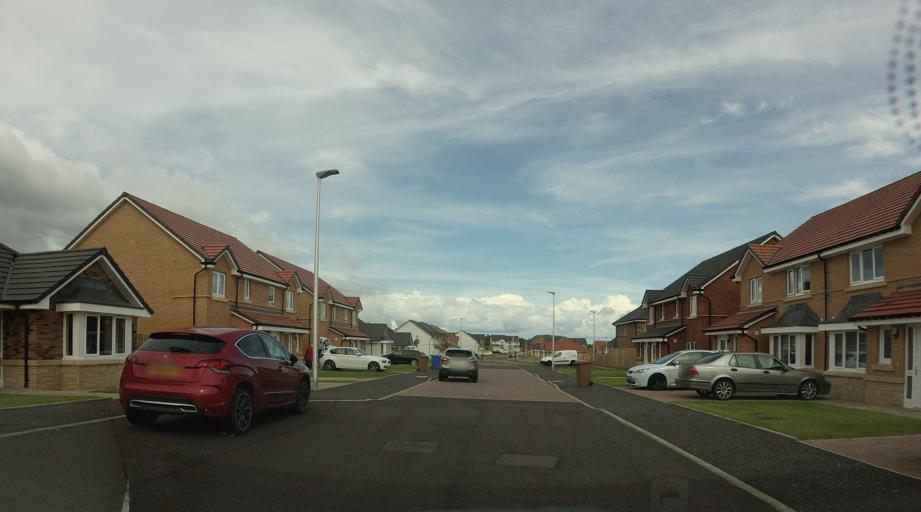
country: GB
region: Scotland
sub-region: West Lothian
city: Broxburn
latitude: 55.9377
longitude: -3.4985
